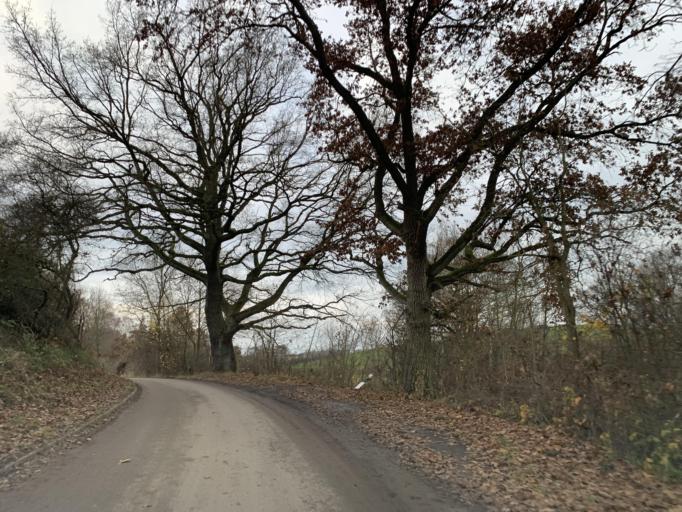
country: DE
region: Mecklenburg-Vorpommern
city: Carpin
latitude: 53.3990
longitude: 13.2170
